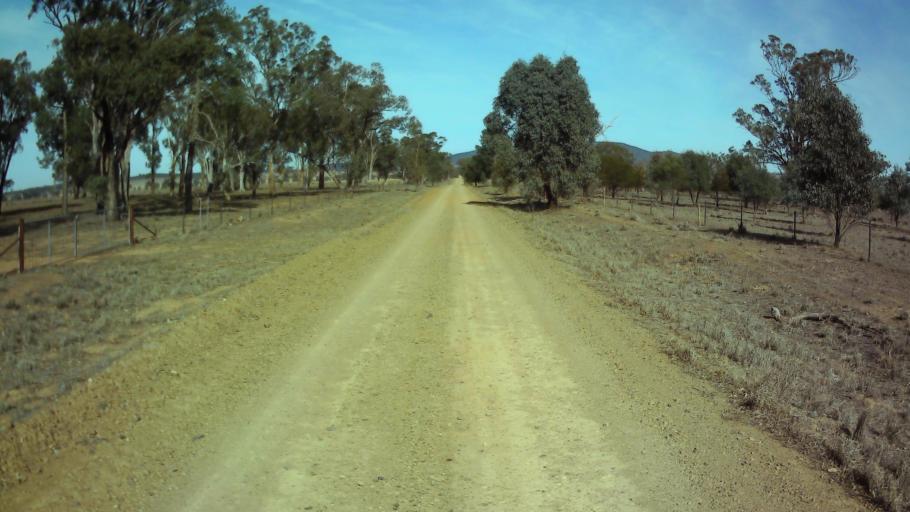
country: AU
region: New South Wales
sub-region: Weddin
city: Grenfell
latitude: -33.7527
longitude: 148.0108
